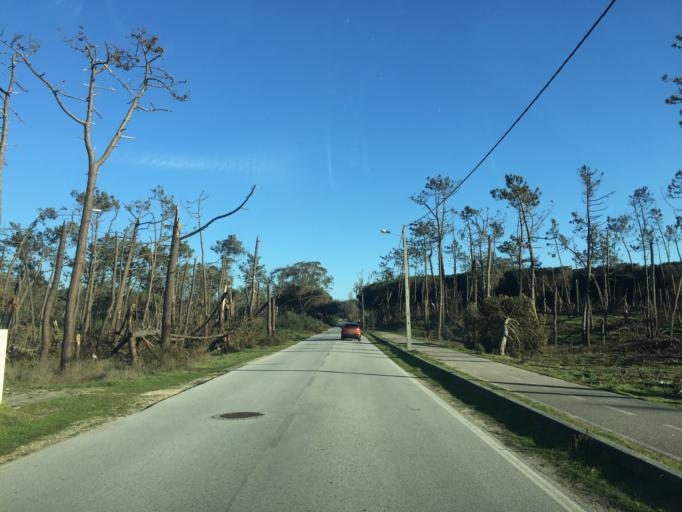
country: PT
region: Coimbra
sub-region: Figueira da Foz
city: Lavos
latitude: 40.0871
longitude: -8.8718
